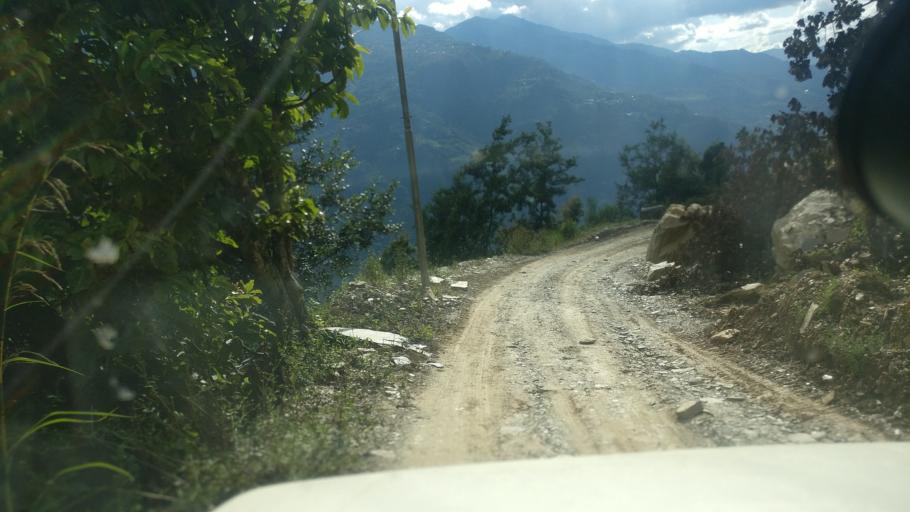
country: NP
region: Western Region
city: Baglung
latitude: 28.2642
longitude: 83.6435
